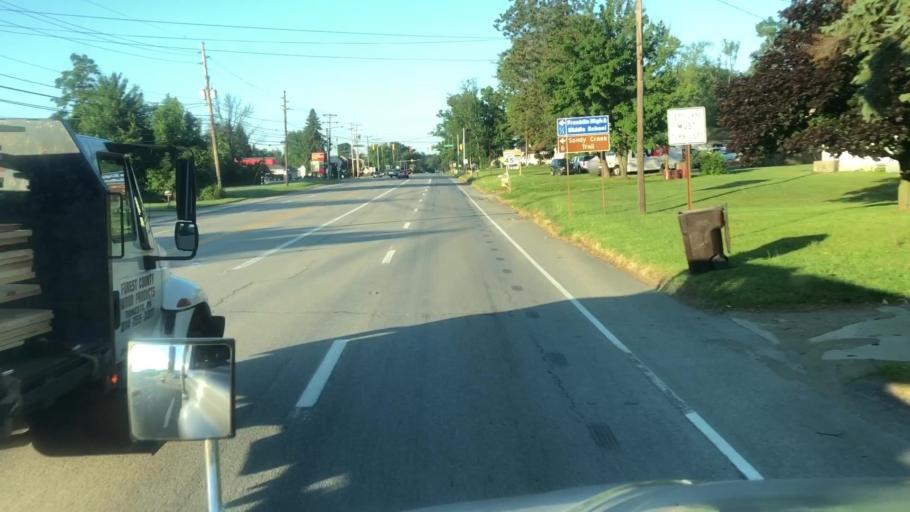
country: US
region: Pennsylvania
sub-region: Venango County
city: Franklin
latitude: 41.3759
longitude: -79.8538
